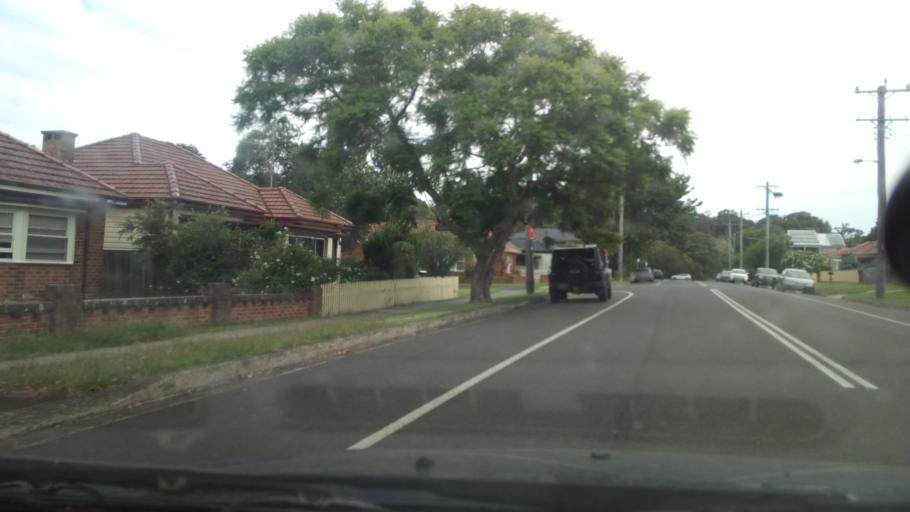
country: AU
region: New South Wales
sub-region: Wollongong
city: Gwynneville
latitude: -34.4140
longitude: 150.8794
